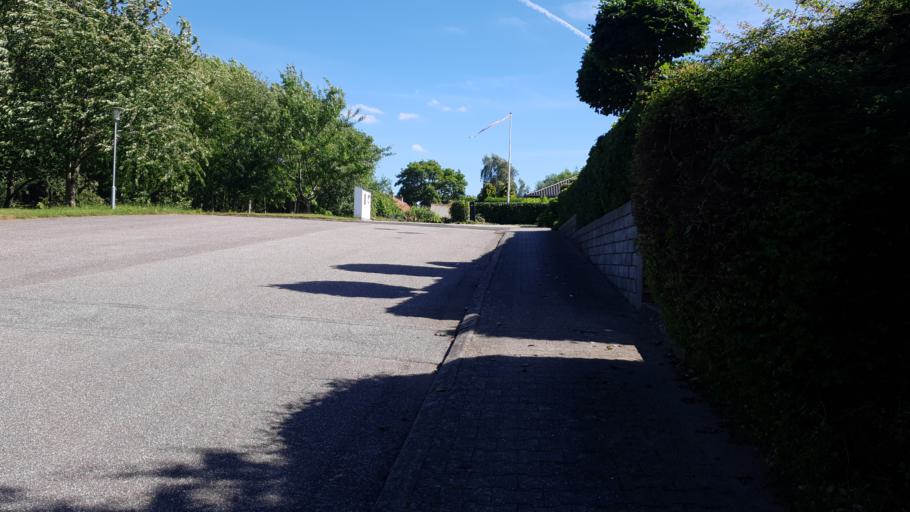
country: DK
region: South Denmark
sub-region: Fredericia Kommune
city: Snoghoj
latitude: 55.5339
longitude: 9.7333
